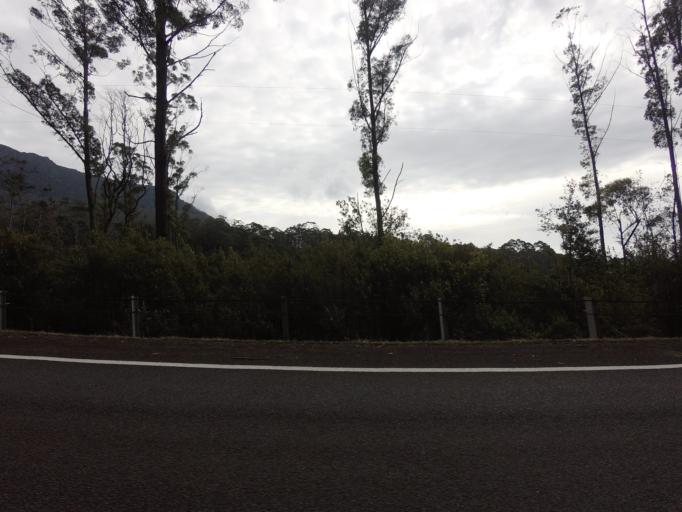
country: AU
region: Tasmania
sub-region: Meander Valley
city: Deloraine
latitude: -41.6482
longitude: 146.7215
